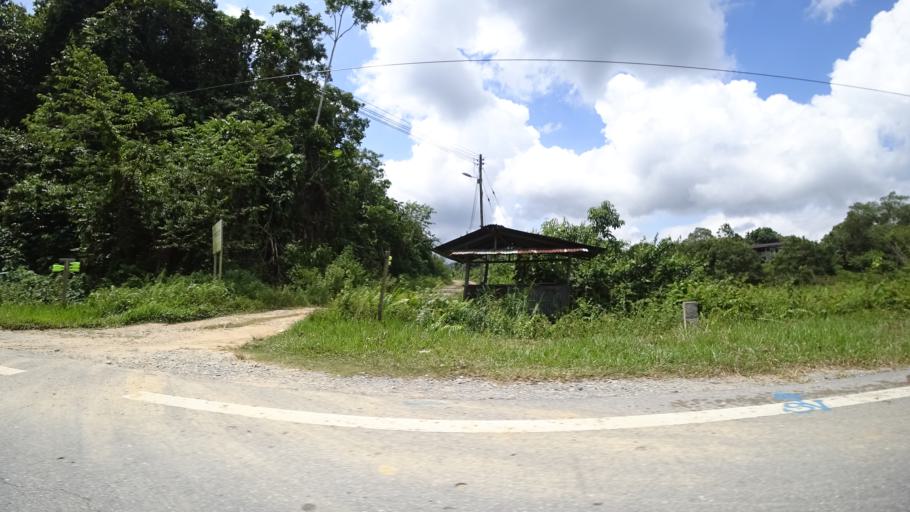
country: BN
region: Tutong
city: Tutong
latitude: 4.7060
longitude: 114.7969
